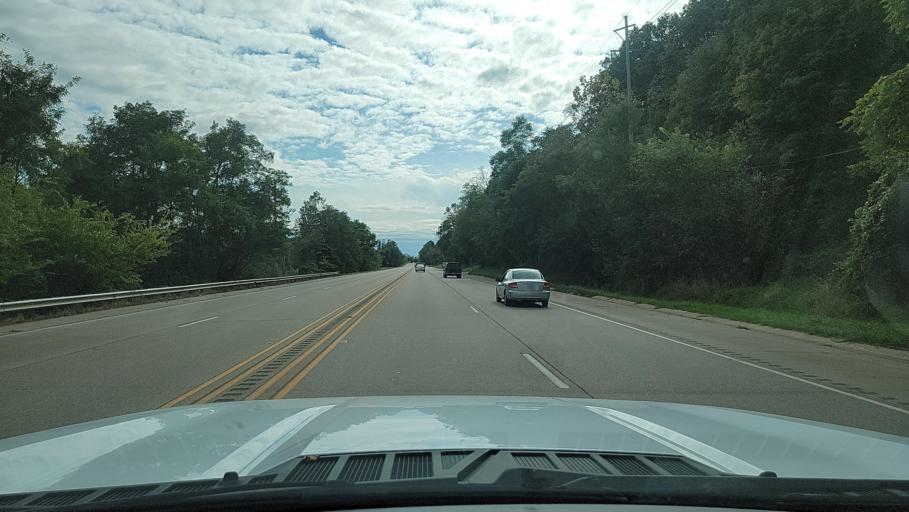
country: US
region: Illinois
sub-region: Peoria County
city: Bartonville
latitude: 40.6210
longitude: -89.6562
